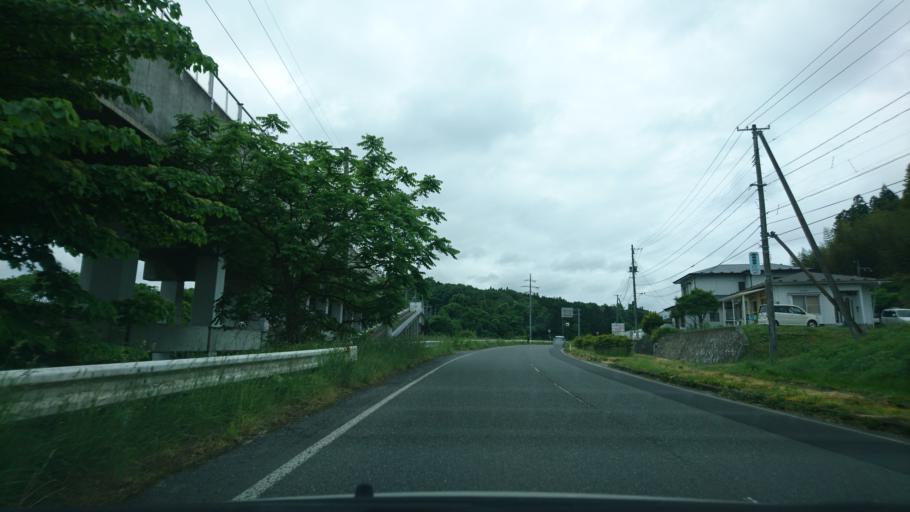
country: JP
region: Iwate
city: Ichinoseki
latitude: 38.8992
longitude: 141.1289
